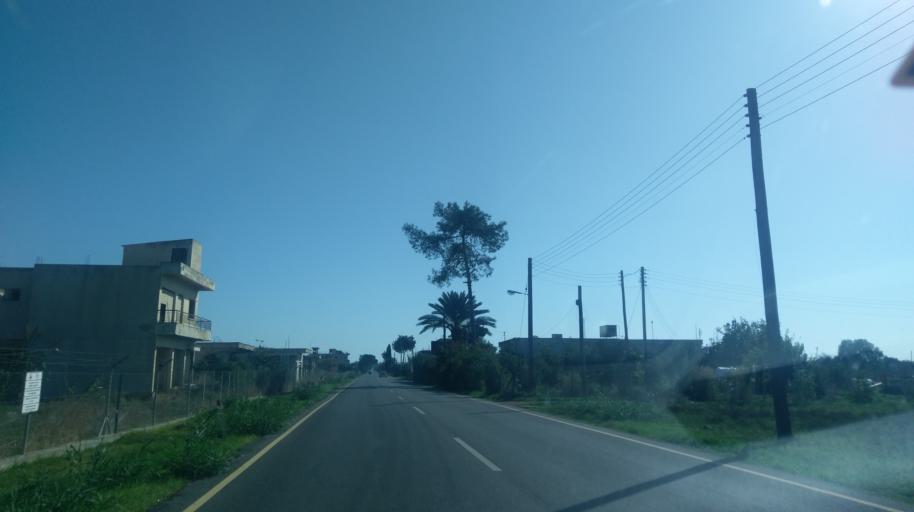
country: CY
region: Ammochostos
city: Famagusta
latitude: 35.0971
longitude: 33.9507
